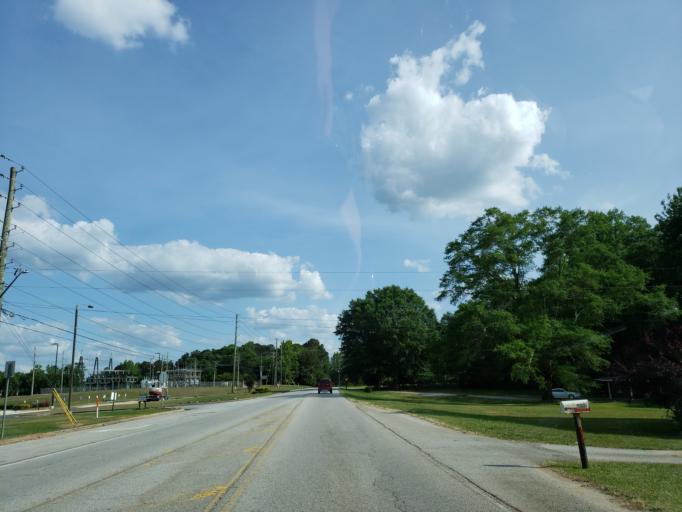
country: US
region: Georgia
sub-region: Carroll County
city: Carrollton
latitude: 33.6060
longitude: -85.0797
